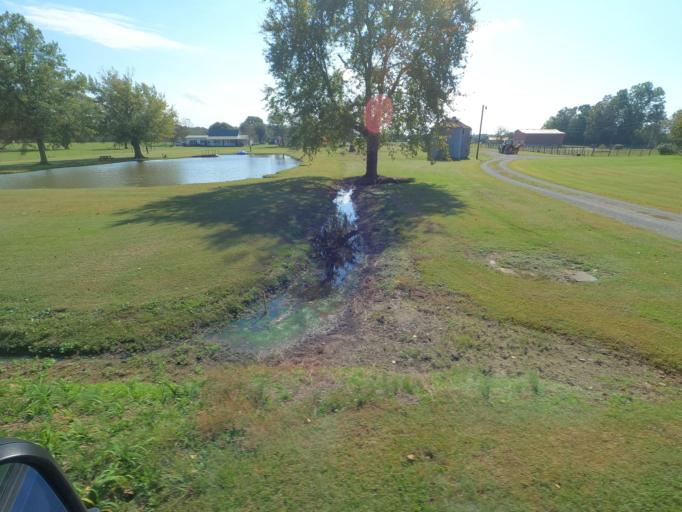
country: US
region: Tennessee
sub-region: Cheatham County
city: Pleasant View
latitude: 36.4428
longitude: -87.1092
